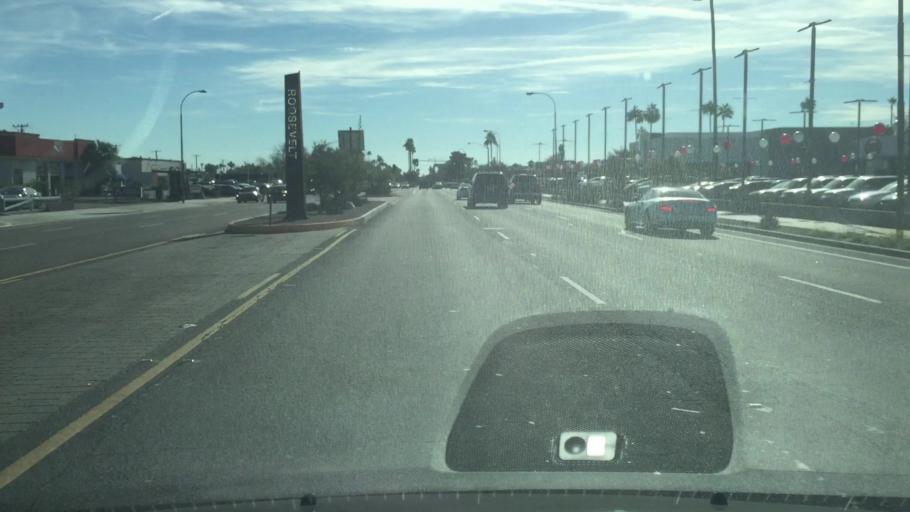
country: US
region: Arizona
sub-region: Maricopa County
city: Tempe
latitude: 33.4601
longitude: -111.9264
